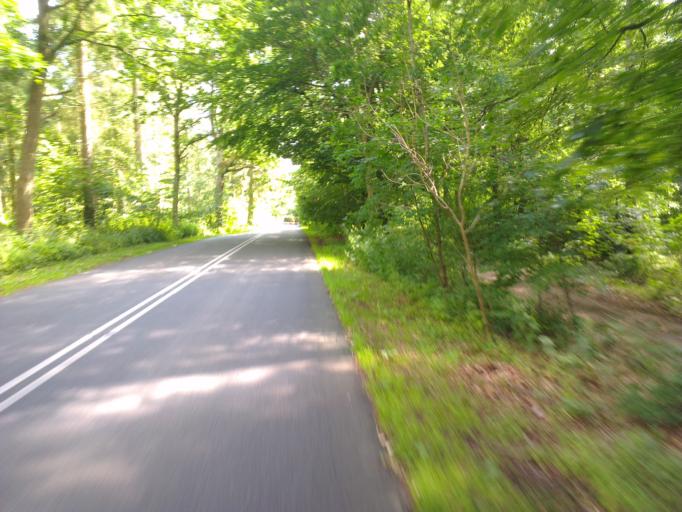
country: DK
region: Zealand
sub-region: Lejre Kommune
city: Ejby
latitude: 55.7352
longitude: 11.8832
